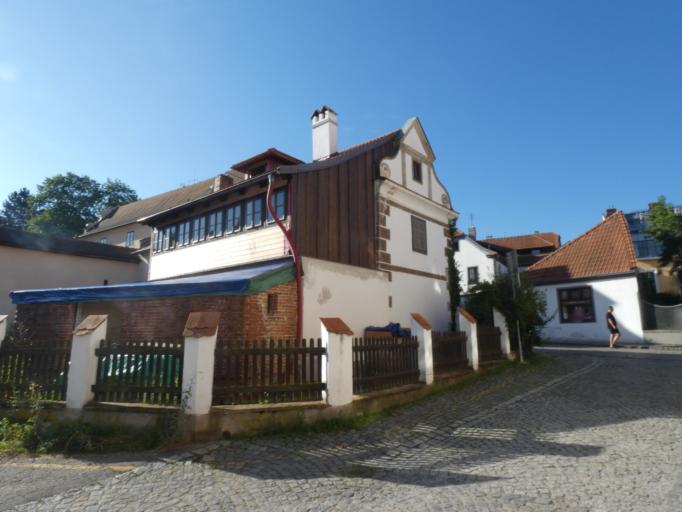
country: CZ
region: Jihocesky
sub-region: Okres Cesky Krumlov
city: Cesky Krumlov
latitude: 48.8088
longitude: 14.3166
